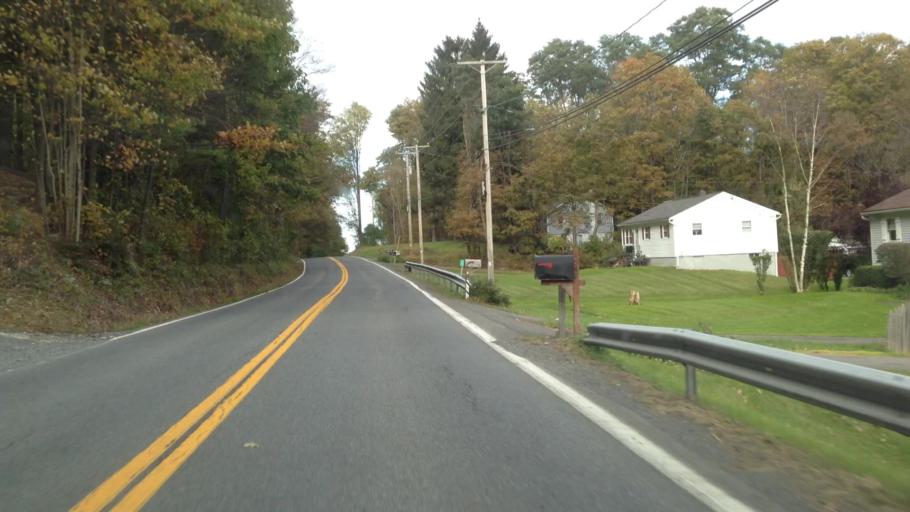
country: US
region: New York
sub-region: Ulster County
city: Rosendale Village
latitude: 41.8657
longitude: -74.0300
